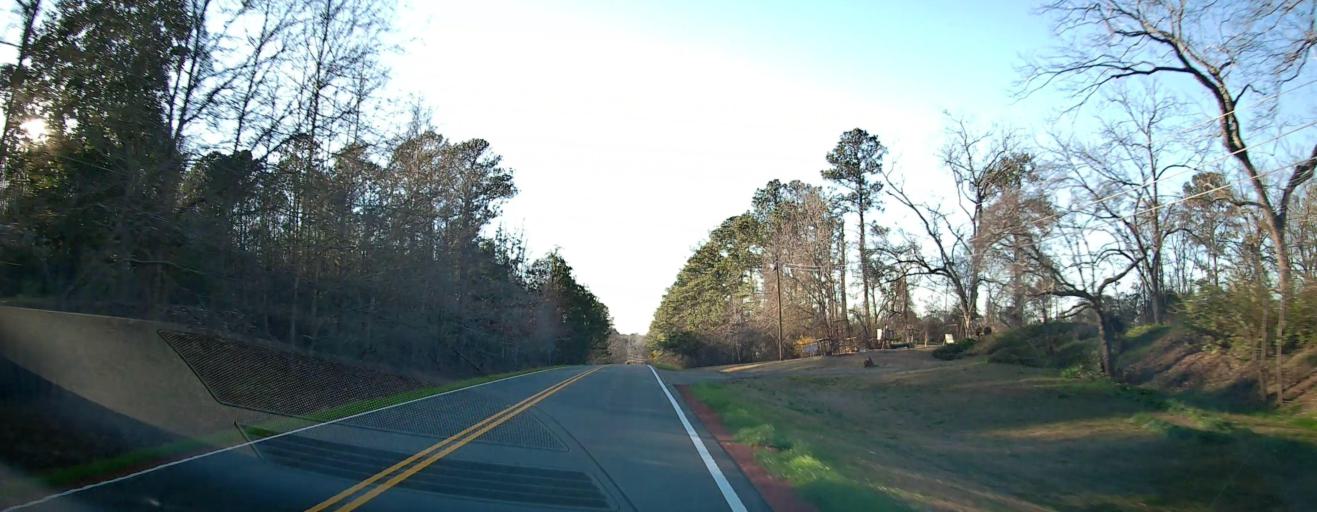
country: US
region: Georgia
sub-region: Meriwether County
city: Manchester
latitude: 32.8922
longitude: -84.7036
